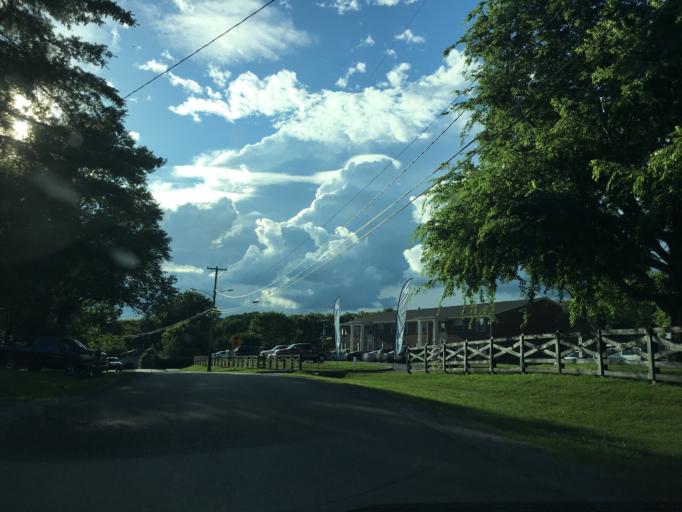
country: US
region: Tennessee
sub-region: Davidson County
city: Oak Hill
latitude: 36.0675
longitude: -86.7290
